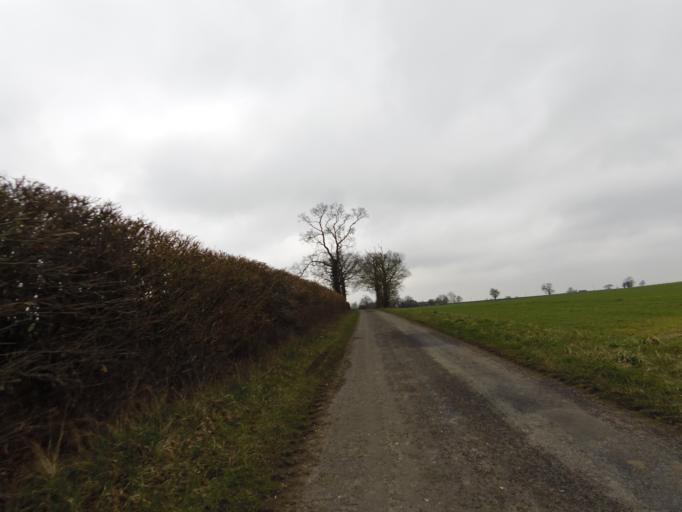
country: GB
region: England
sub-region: Suffolk
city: Framlingham
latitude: 52.2360
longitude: 1.3883
